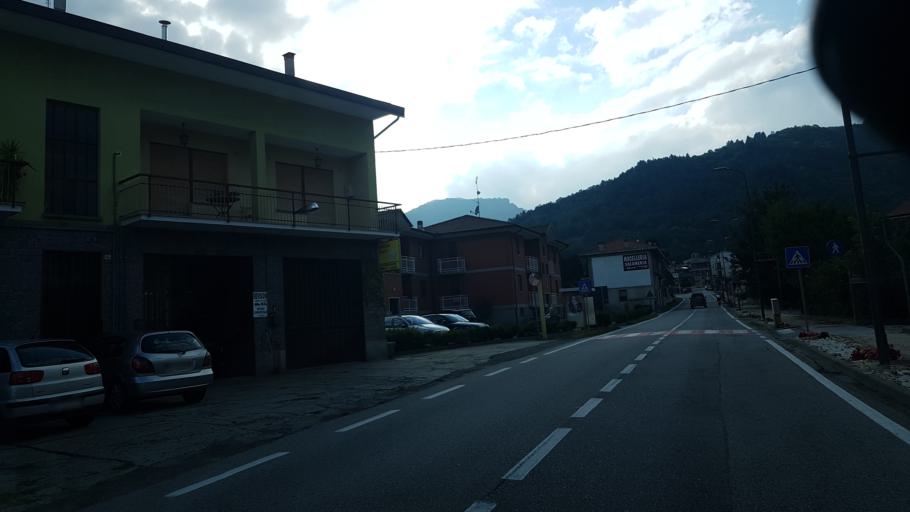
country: IT
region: Piedmont
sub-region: Provincia di Cuneo
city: Brossasco
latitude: 44.5682
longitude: 7.3667
